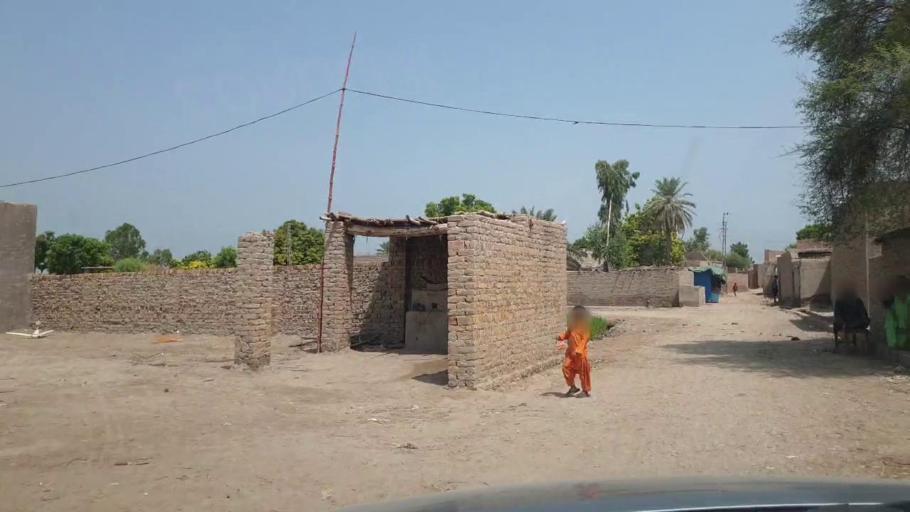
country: PK
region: Sindh
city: Madeji
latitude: 27.8094
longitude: 68.5181
